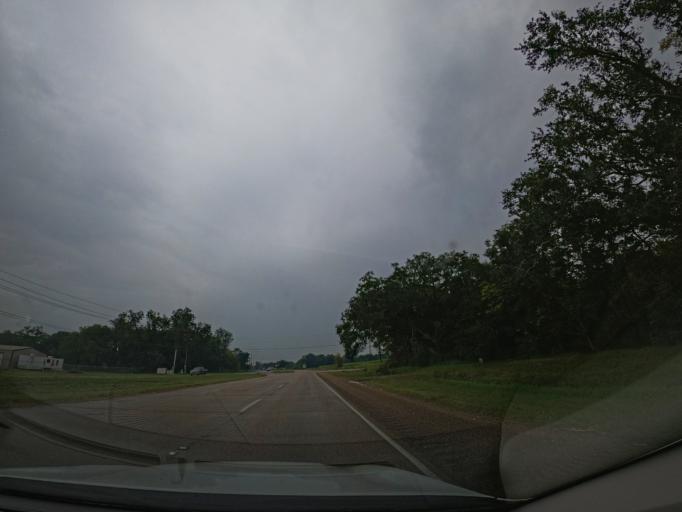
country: US
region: Louisiana
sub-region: Iberia Parish
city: New Iberia
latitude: 29.9853
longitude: -91.8863
